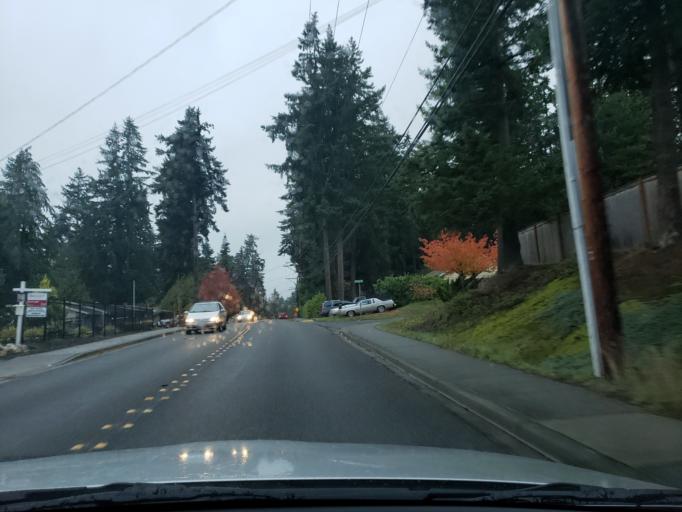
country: US
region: Washington
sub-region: Snohomish County
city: Lynnwood
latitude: 47.8392
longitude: -122.3109
